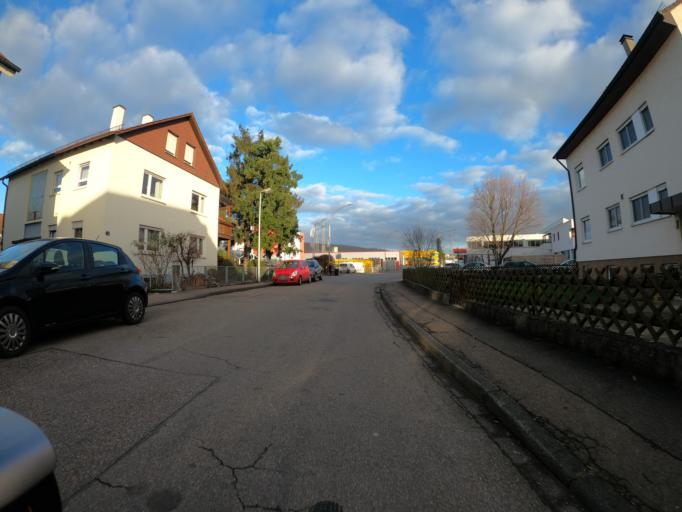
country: DE
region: Baden-Wuerttemberg
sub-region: Regierungsbezirk Stuttgart
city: Deizisau
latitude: 48.7138
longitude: 9.3909
